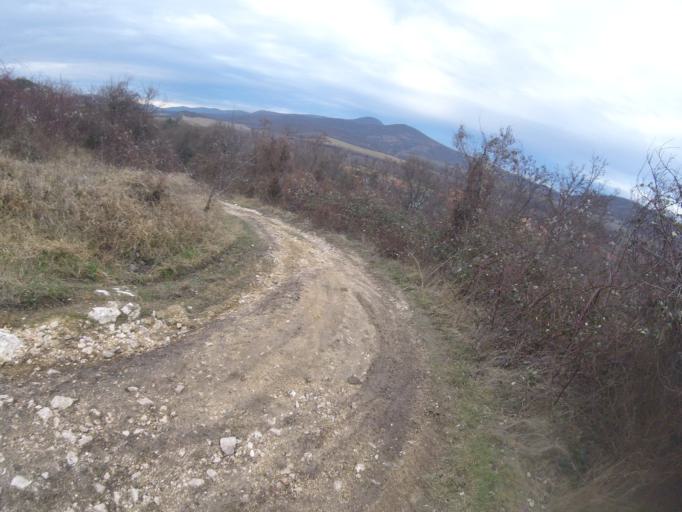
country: HU
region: Pest
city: Nagykovacsi
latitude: 47.6491
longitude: 18.9930
